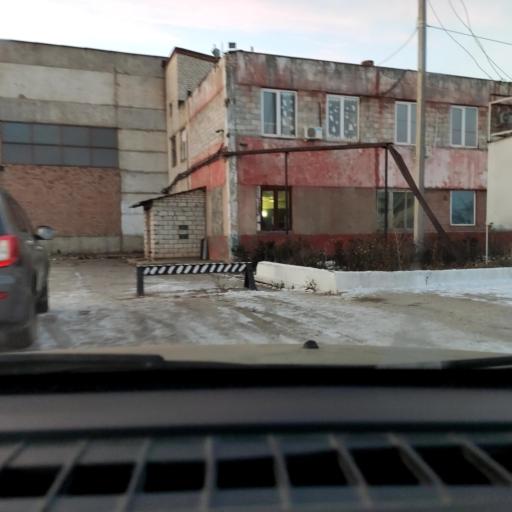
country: RU
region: Samara
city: Tol'yatti
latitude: 53.5790
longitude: 49.2656
